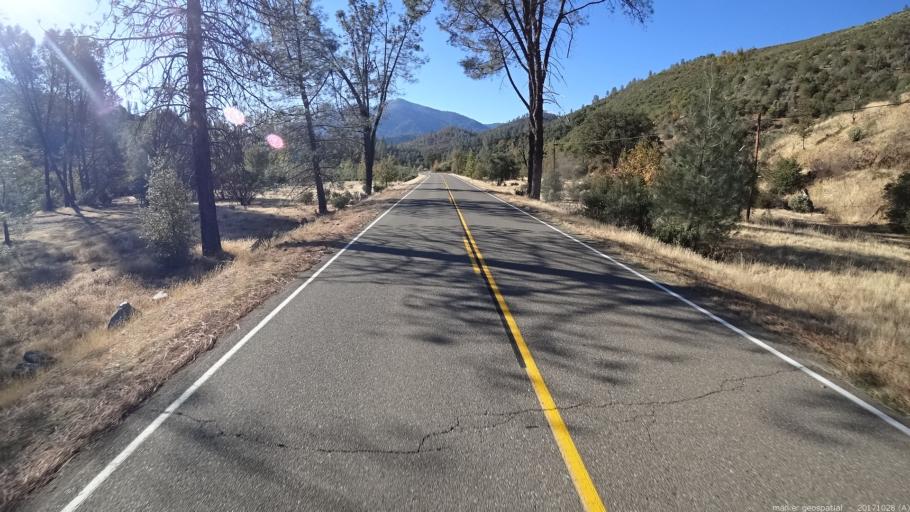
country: US
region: California
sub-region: Shasta County
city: Shasta
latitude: 40.6756
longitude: -122.6356
